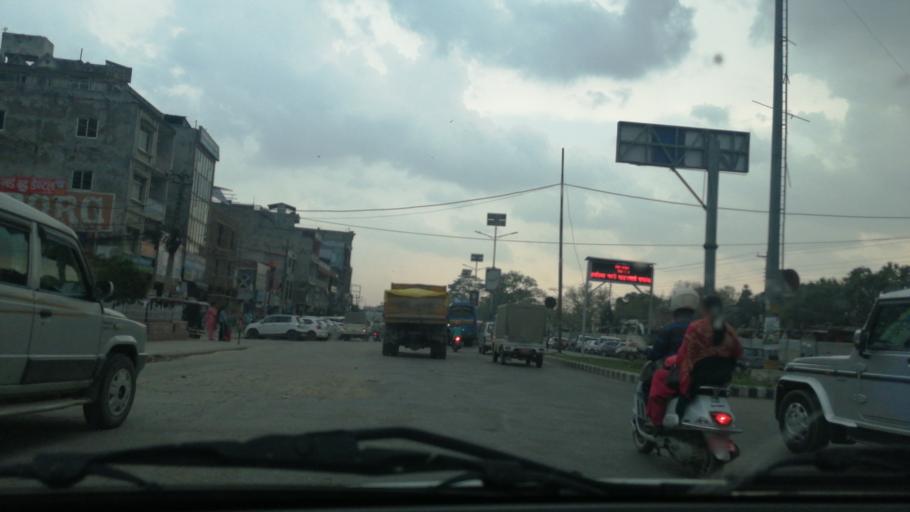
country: NP
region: Western Region
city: Butwal
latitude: 27.6983
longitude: 83.4654
